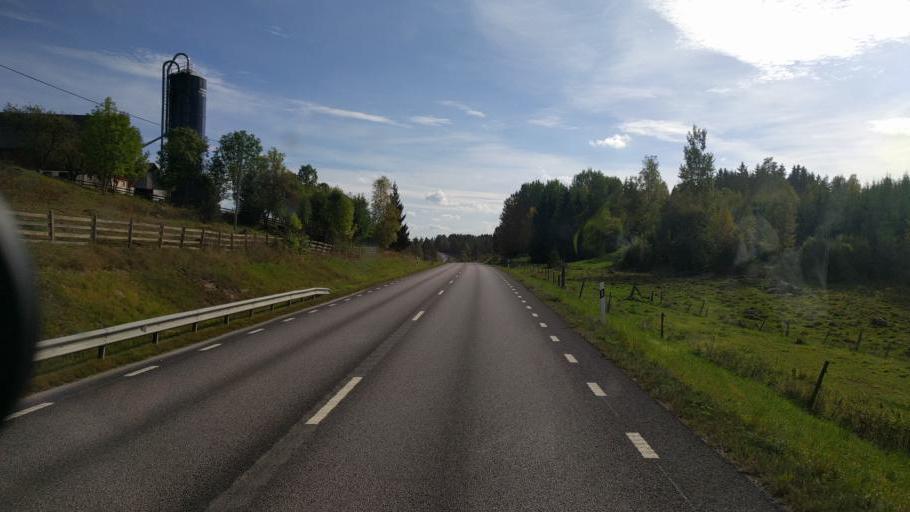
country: SE
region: OEstergoetland
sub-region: Kinda Kommun
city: Kisa
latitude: 57.9291
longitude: 15.6720
